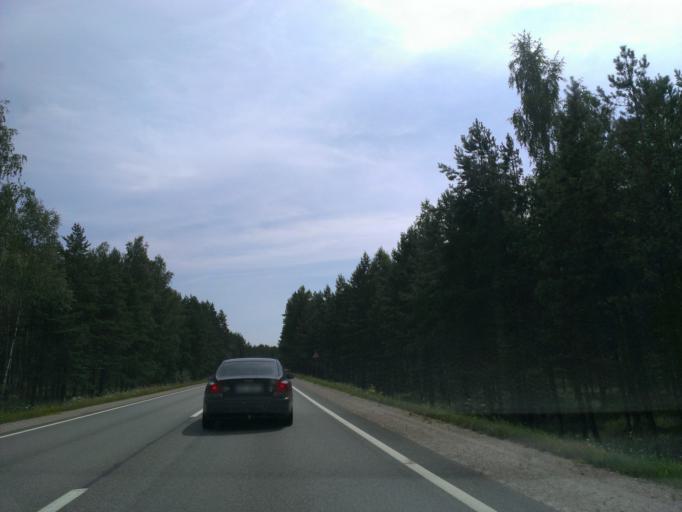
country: LV
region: Riga
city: Bergi
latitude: 56.9618
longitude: 24.3730
